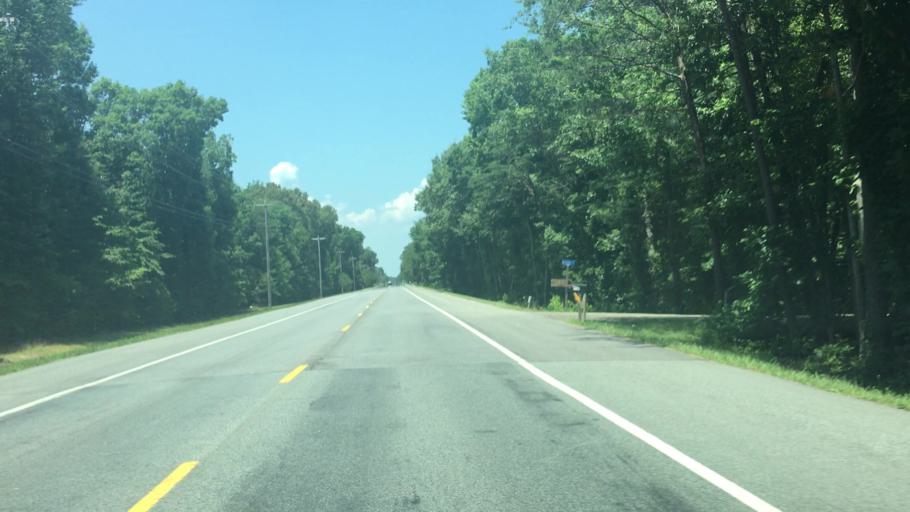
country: US
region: Maryland
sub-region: Saint Mary's County
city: Mechanicsville
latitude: 38.3855
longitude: -76.8209
